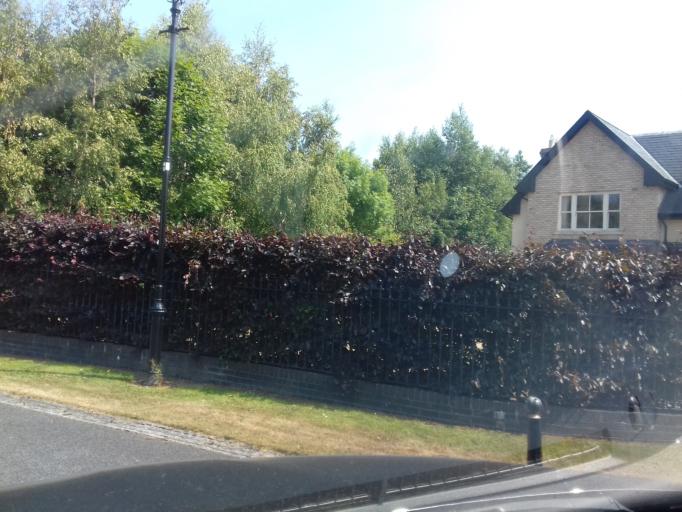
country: IE
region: Leinster
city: Kinsealy-Drinan
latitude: 53.4452
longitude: -6.1810
